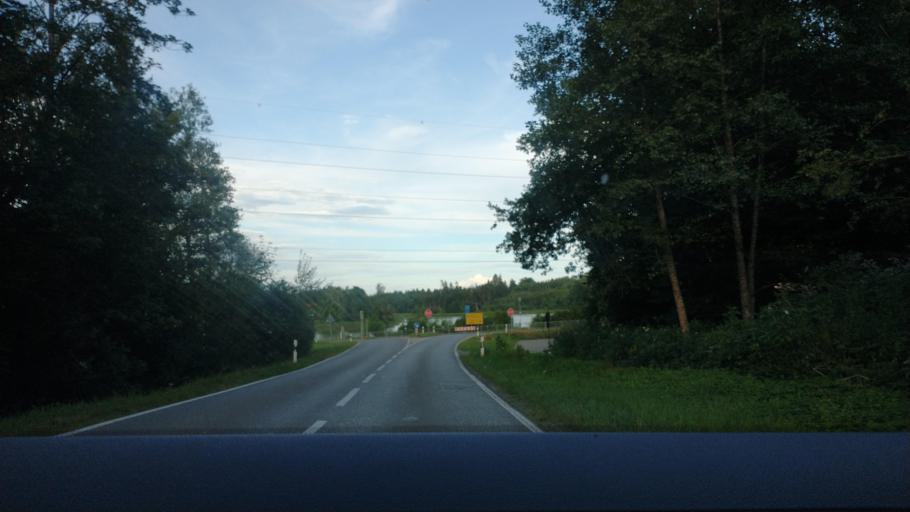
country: DE
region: Bavaria
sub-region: Swabia
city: Hergensweiler
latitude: 47.6316
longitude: 9.7520
